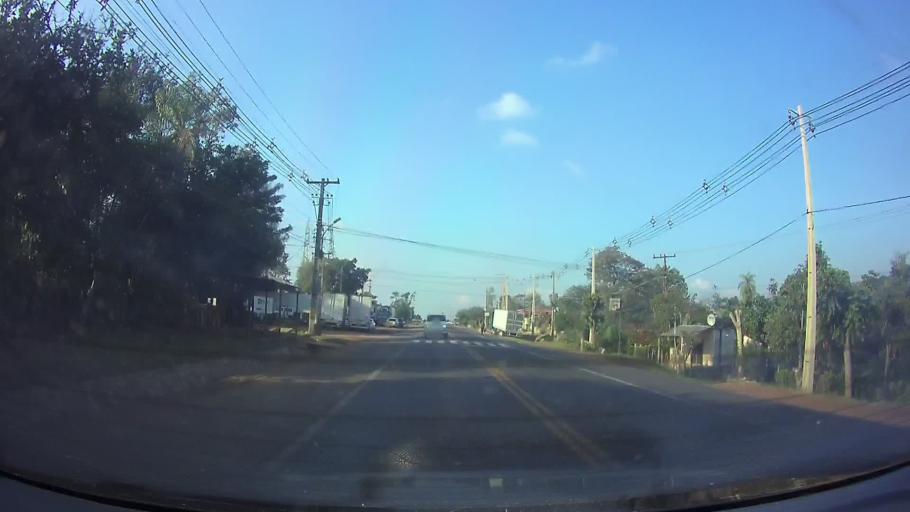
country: PY
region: Central
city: Limpio
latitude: -25.1388
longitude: -57.4540
